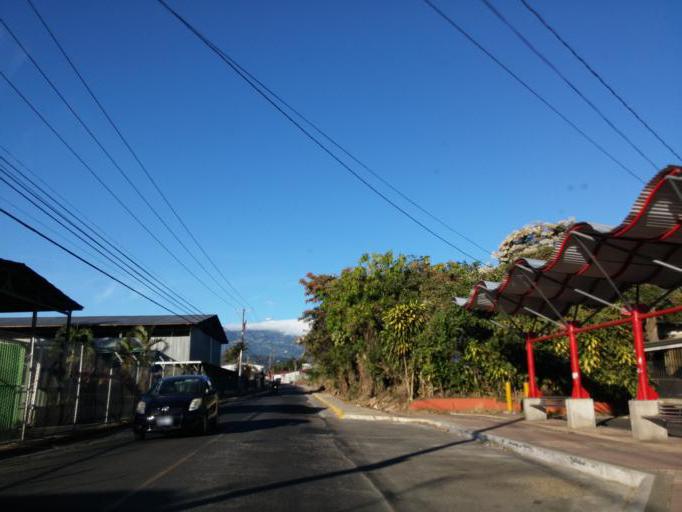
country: CR
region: Alajuela
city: Alajuela
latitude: 10.0089
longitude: -84.2032
